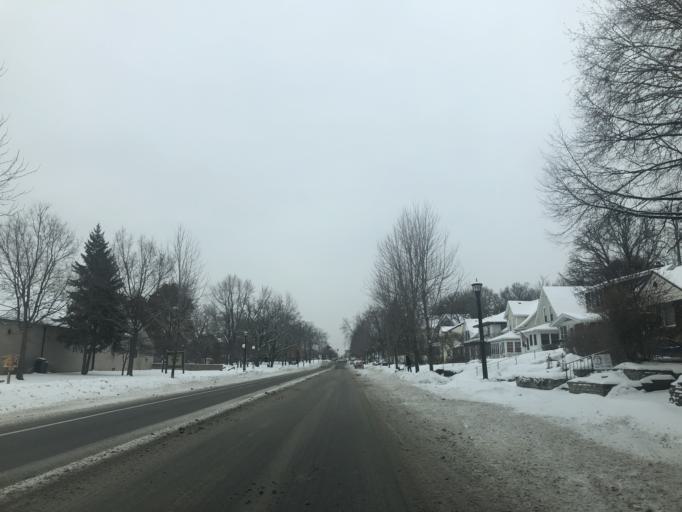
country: US
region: Minnesota
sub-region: Hennepin County
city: Richfield
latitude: 44.9300
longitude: -93.2780
